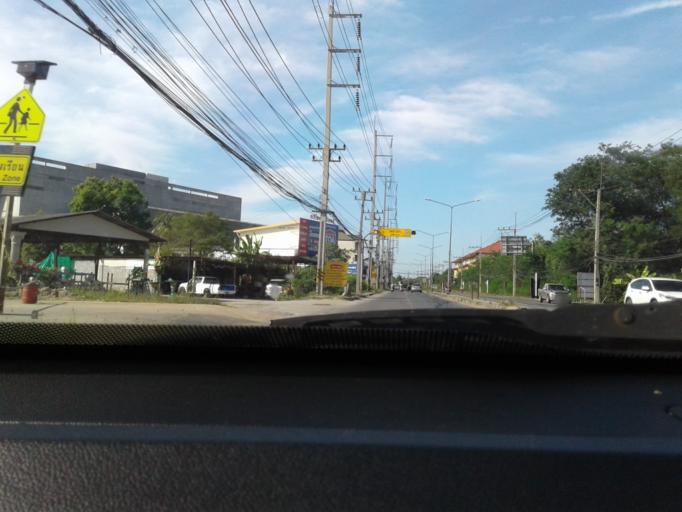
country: TH
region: Nakhon Pathom
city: Salaya
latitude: 13.8137
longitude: 100.3222
